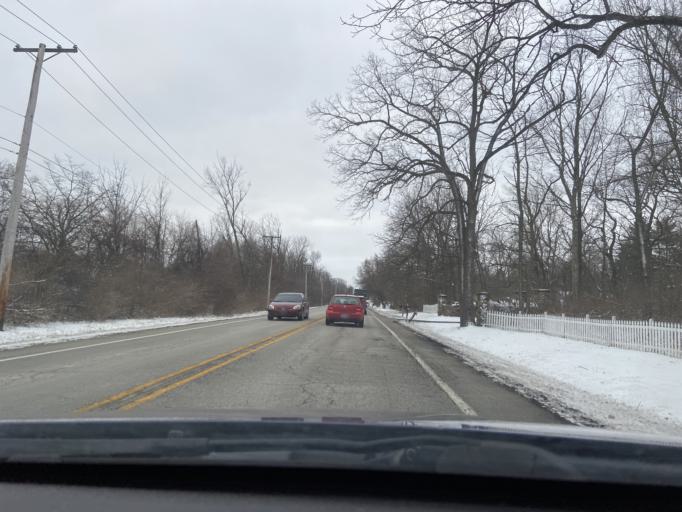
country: US
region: Illinois
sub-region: Lake County
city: Round Lake Park
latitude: 42.3672
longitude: -88.0680
